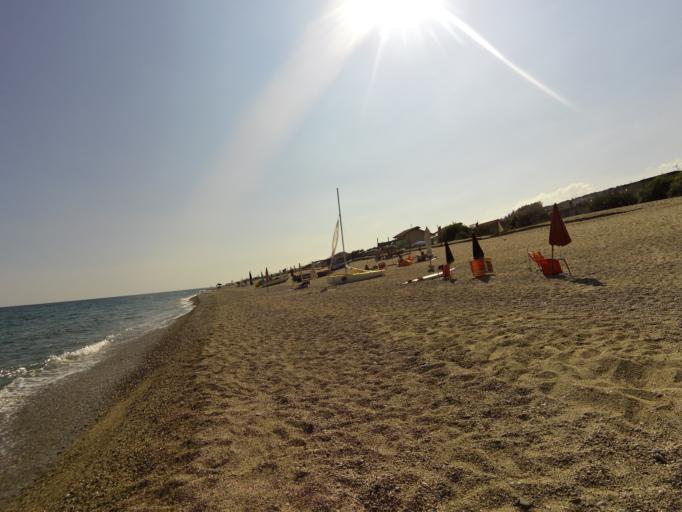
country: IT
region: Calabria
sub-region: Provincia di Reggio Calabria
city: Riace Marina
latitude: 38.3998
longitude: 16.5432
